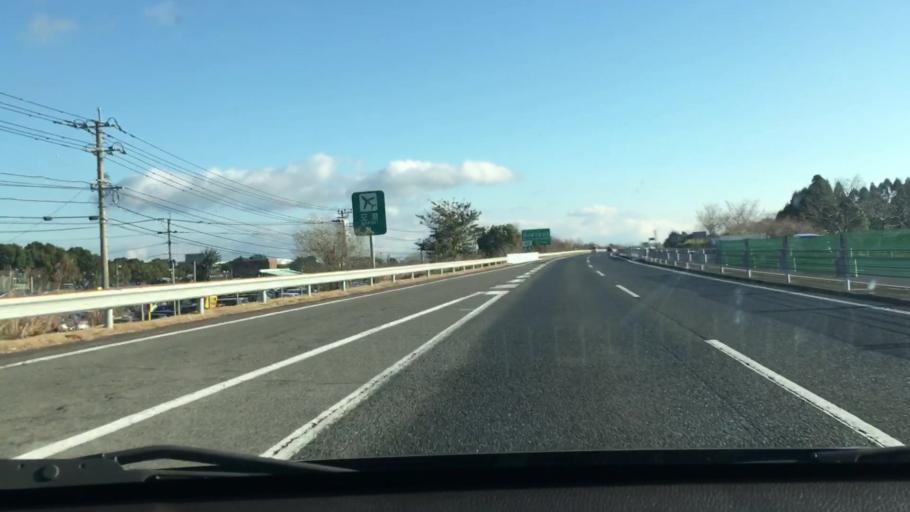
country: JP
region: Kagoshima
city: Kajiki
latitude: 31.7999
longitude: 130.7133
